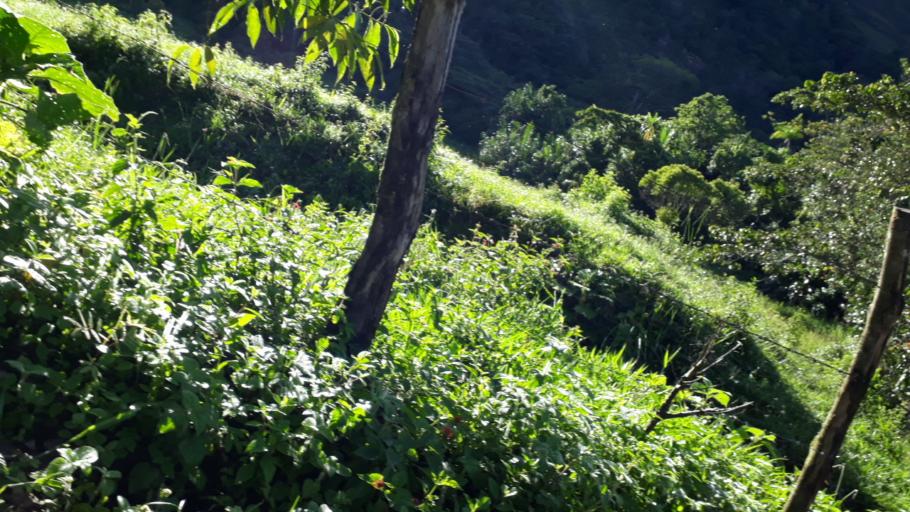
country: CO
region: Casanare
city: Nunchia
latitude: 5.6455
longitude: -72.4244
